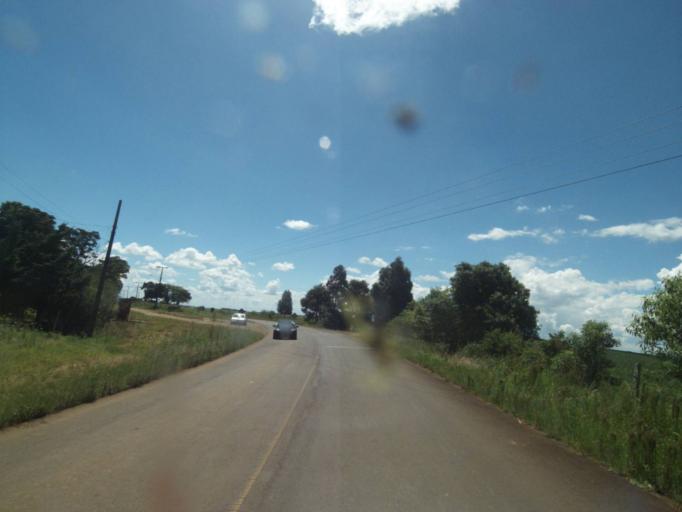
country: BR
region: Parana
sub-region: Pinhao
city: Pinhao
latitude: -25.8139
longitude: -52.0440
